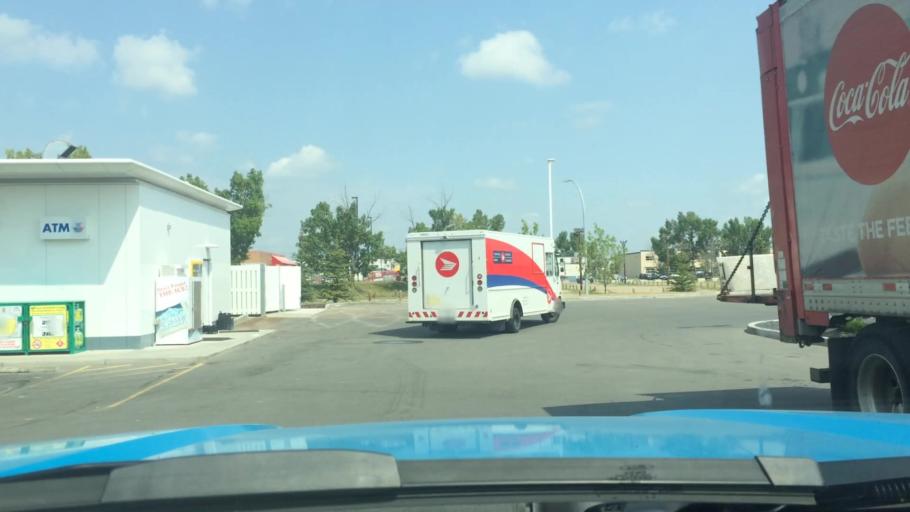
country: CA
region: Alberta
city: Calgary
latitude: 51.0977
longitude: -114.0319
